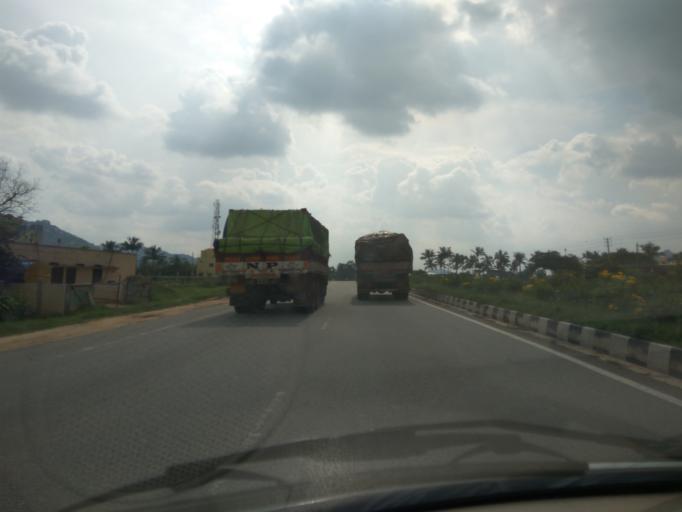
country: IN
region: Karnataka
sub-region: Kolar
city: Kolar
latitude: 13.1193
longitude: 78.0880
